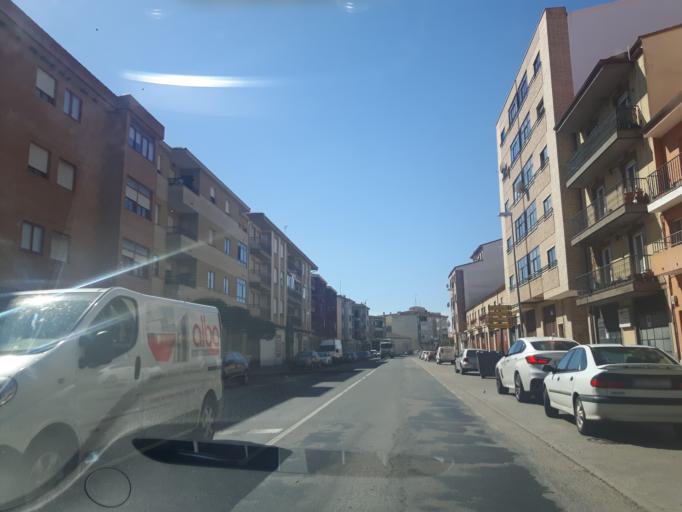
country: ES
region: Castille and Leon
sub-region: Provincia de Salamanca
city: Alba de Tormes
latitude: 40.8260
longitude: -5.5092
